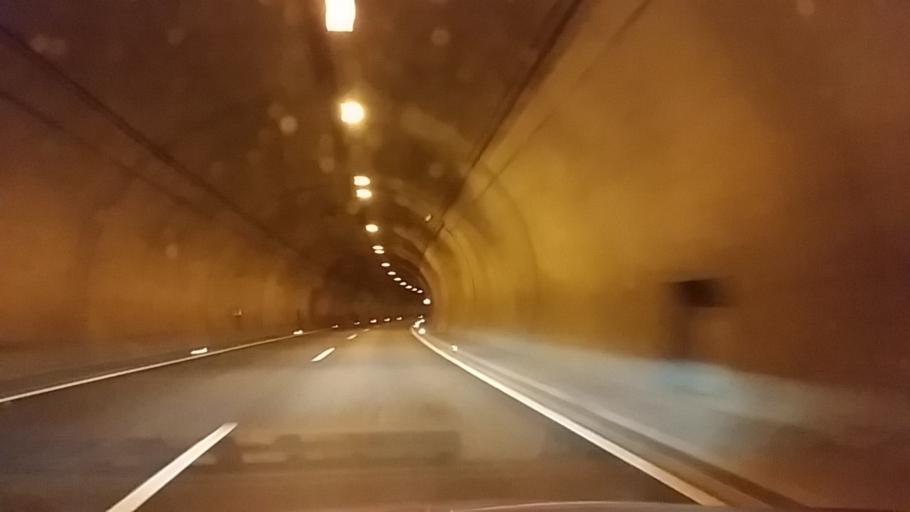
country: DE
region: Thuringia
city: Zella-Mehlis
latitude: 50.6728
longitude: 10.6910
